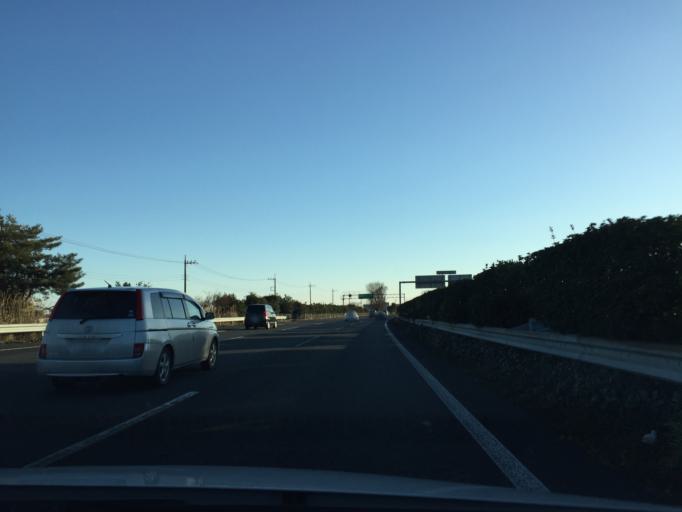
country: JP
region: Tochigi
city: Tochigi
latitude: 36.4203
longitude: 139.7204
